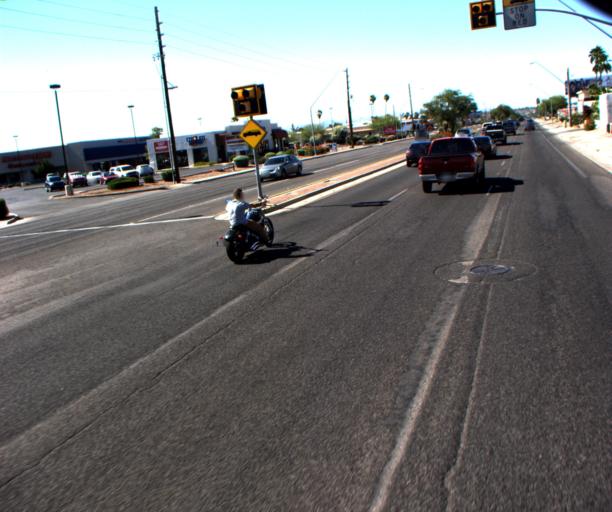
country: US
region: Arizona
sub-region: Pima County
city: Flowing Wells
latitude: 32.2737
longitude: -110.9780
